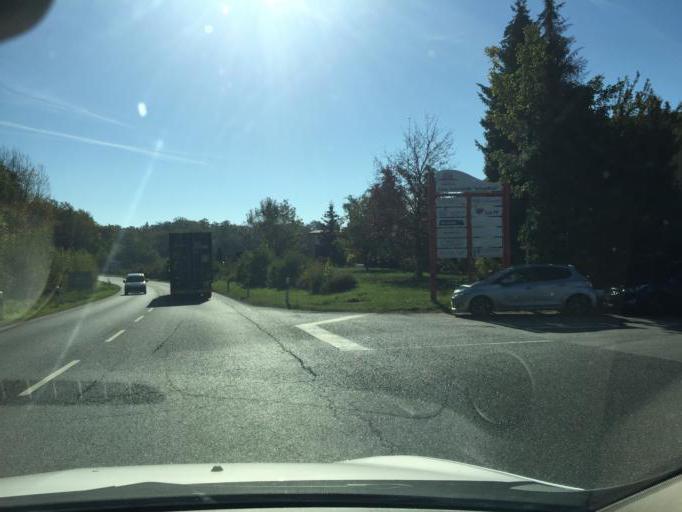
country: LU
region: Luxembourg
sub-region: Canton de Luxembourg
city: Sandweiler
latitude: 49.6080
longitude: 6.2015
